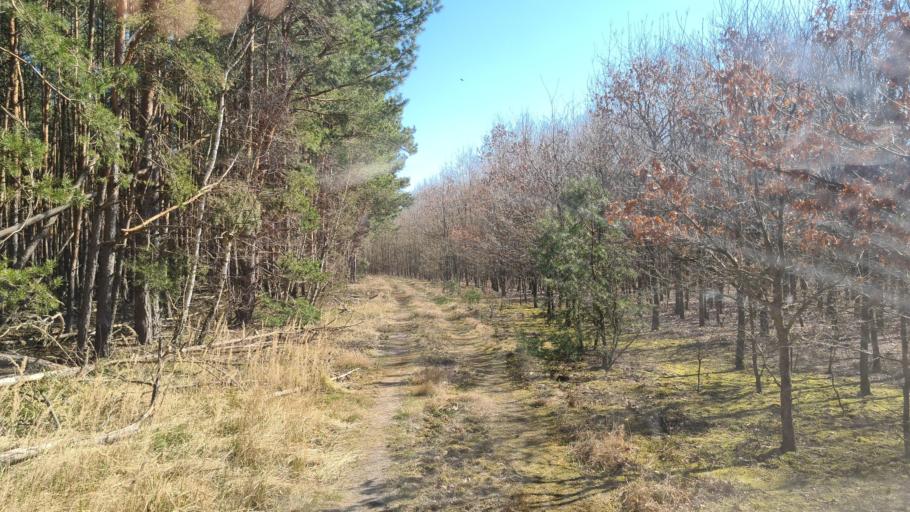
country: DE
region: Brandenburg
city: Finsterwalde
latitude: 51.5830
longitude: 13.7269
